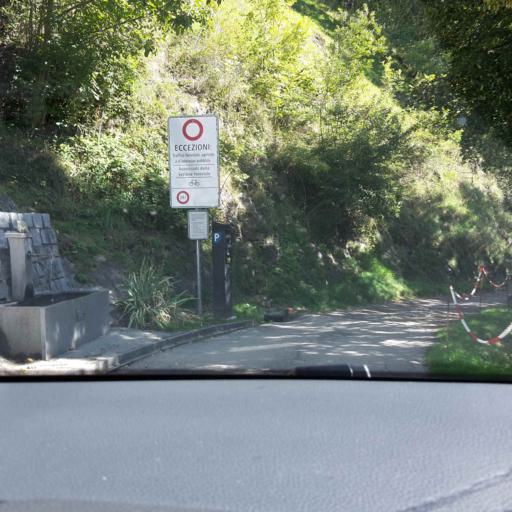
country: CH
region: Ticino
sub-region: Bellinzona District
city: Lumino
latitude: 46.1682
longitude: 9.0873
